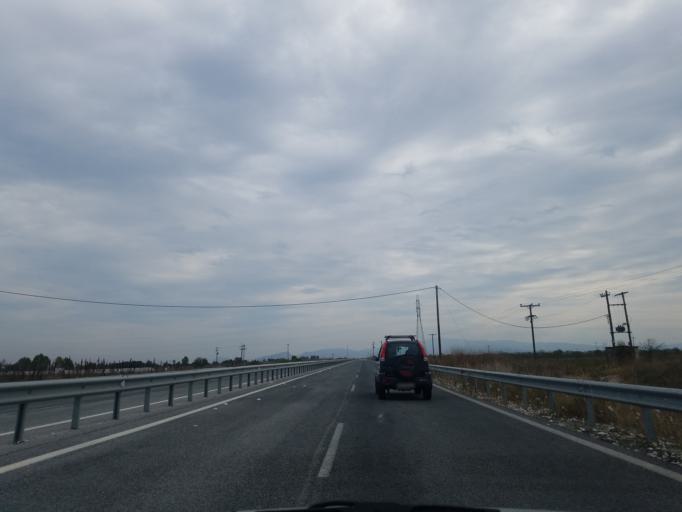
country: GR
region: Thessaly
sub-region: Nomos Kardhitsas
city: Sofades
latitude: 39.2986
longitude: 22.1444
